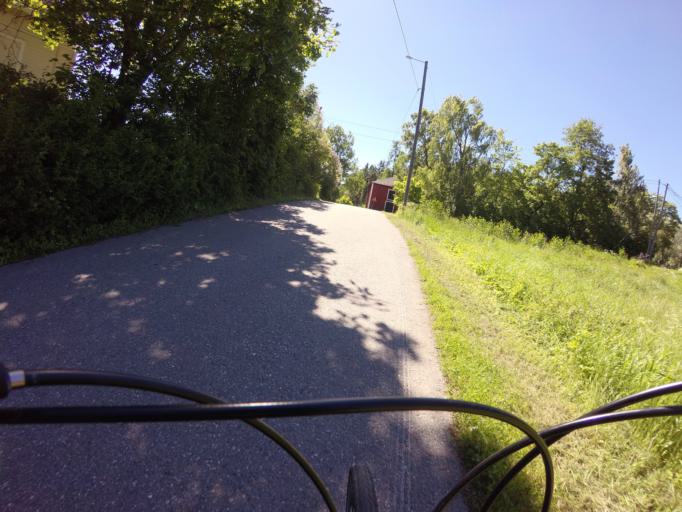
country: FI
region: Varsinais-Suomi
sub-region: Turku
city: Raisio
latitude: 60.4552
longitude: 22.2098
